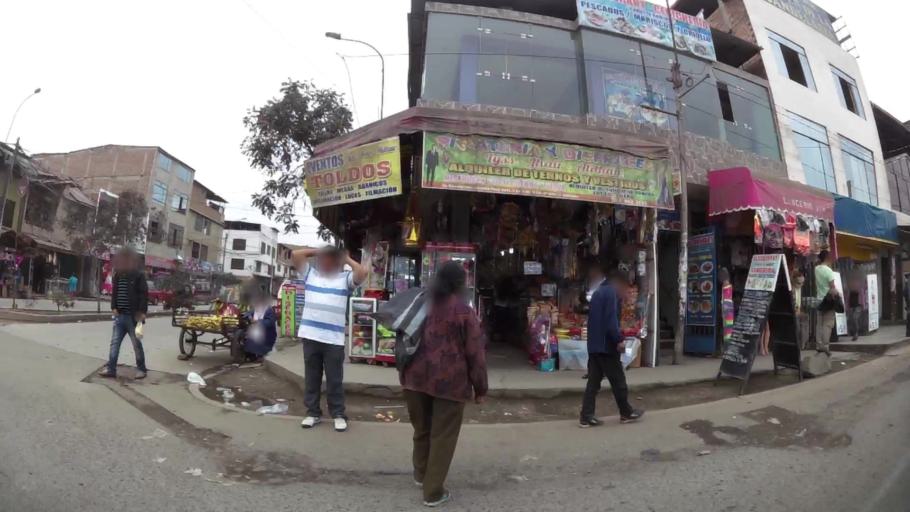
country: PE
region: Lima
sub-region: Lima
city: Surco
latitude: -12.2058
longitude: -76.9412
